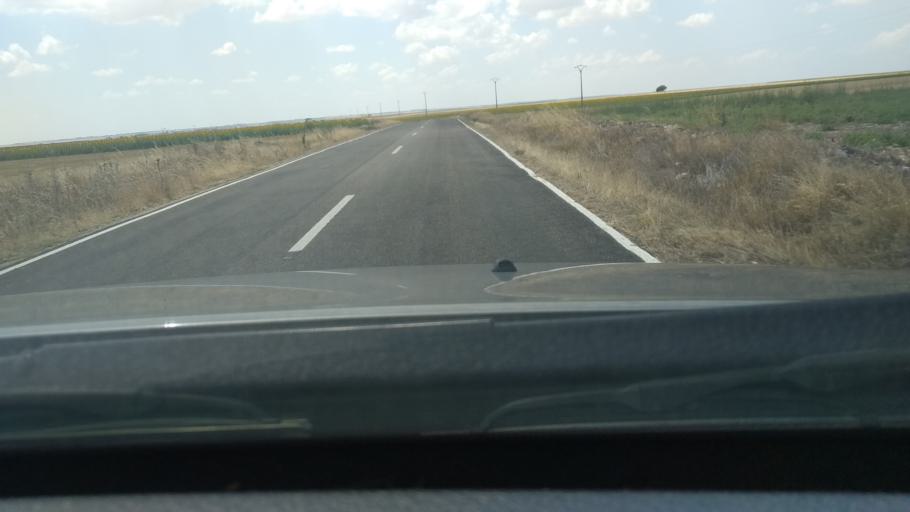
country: ES
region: Castille and Leon
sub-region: Provincia de Burgos
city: Iglesiarrubia
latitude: 41.9414
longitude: -3.8683
